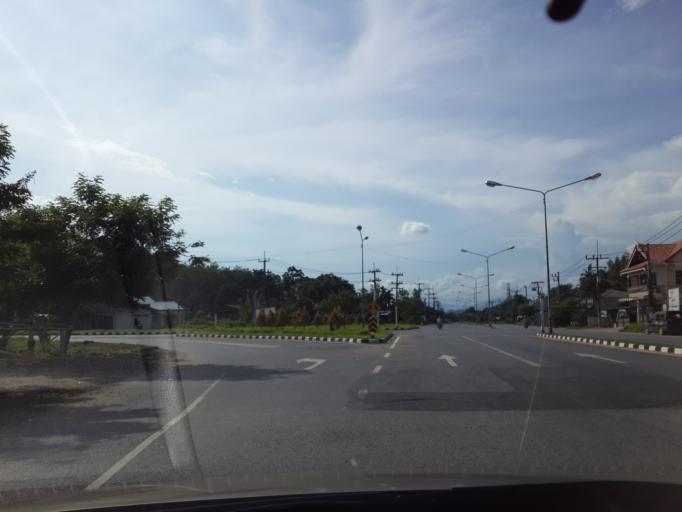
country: TH
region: Yala
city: Yala
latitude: 6.5016
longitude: 101.2881
